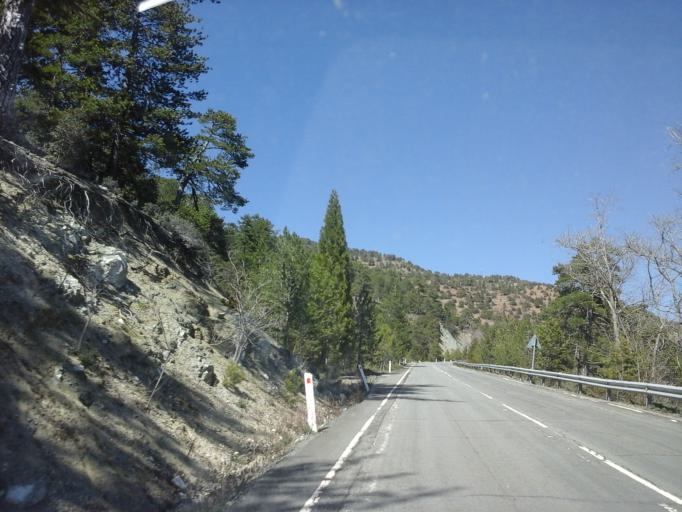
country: CY
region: Lefkosia
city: Kakopetria
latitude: 34.9129
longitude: 32.8686
